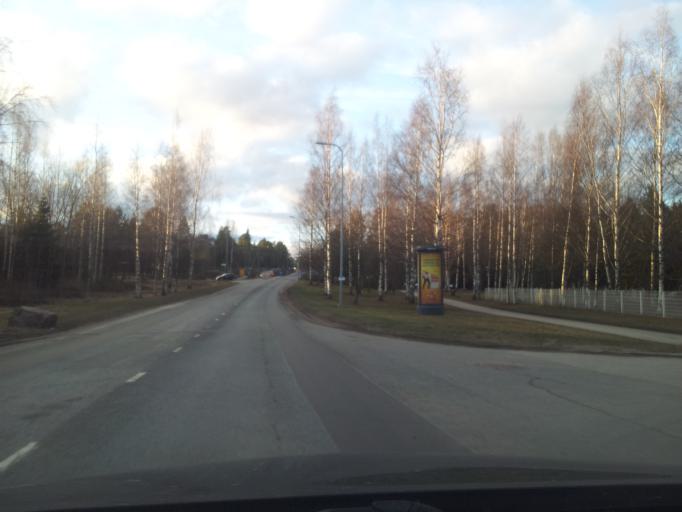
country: FI
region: Uusimaa
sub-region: Helsinki
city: Koukkuniemi
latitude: 60.1710
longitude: 24.7471
